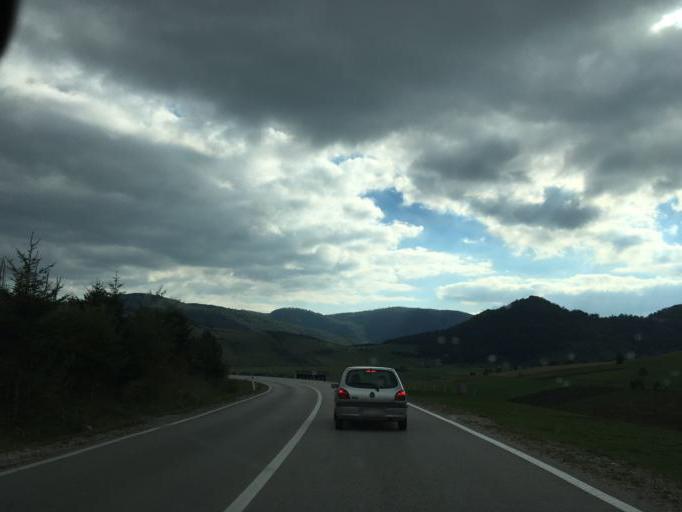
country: BA
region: Federation of Bosnia and Herzegovina
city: Novi Travnik
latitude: 44.1128
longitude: 17.5753
